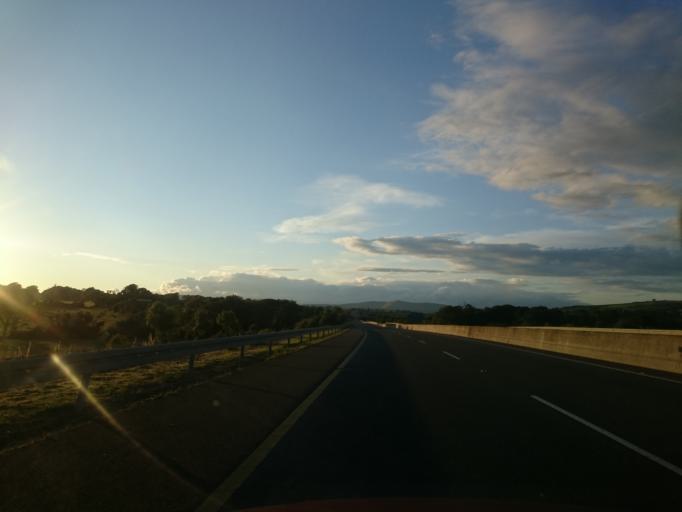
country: IE
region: Leinster
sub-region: Loch Garman
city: Gorey
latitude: 52.6791
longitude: -6.2588
